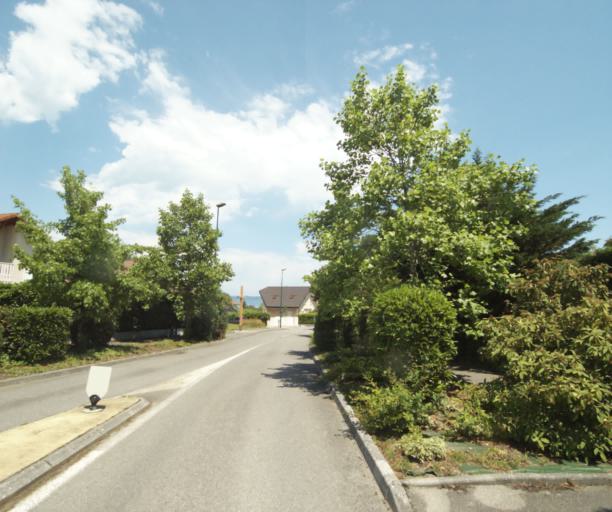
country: FR
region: Rhone-Alpes
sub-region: Departement de la Haute-Savoie
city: Messery
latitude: 46.3665
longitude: 6.3234
